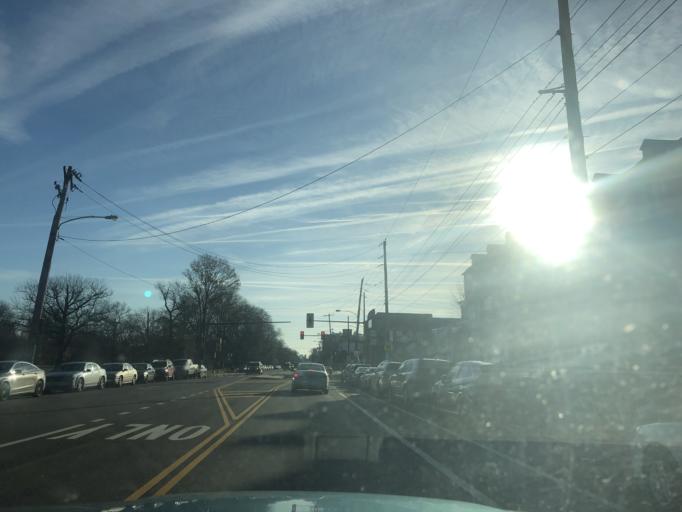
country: US
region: Pennsylvania
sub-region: Montgomery County
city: Bala-Cynwyd
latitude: 39.9811
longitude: -75.2224
